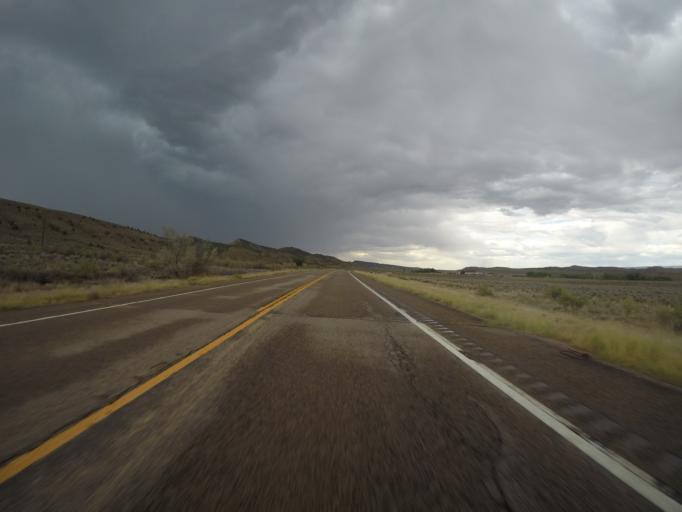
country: US
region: Colorado
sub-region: Rio Blanco County
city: Rangely
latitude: 40.2501
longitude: -108.8694
